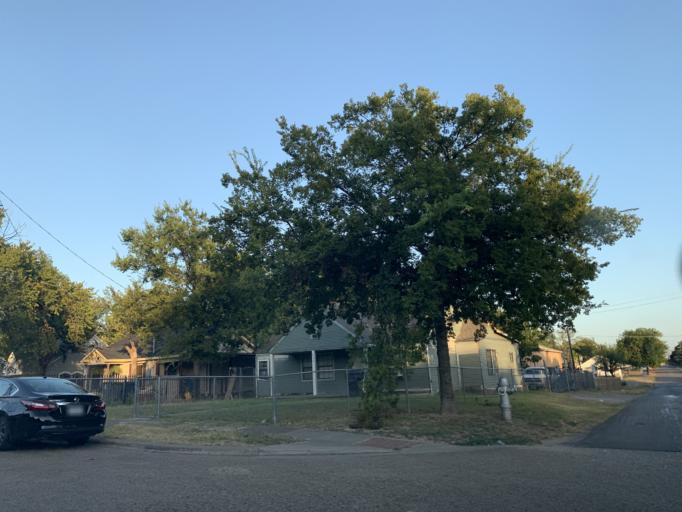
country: US
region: Texas
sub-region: Dallas County
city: Dallas
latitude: 32.7029
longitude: -96.8004
